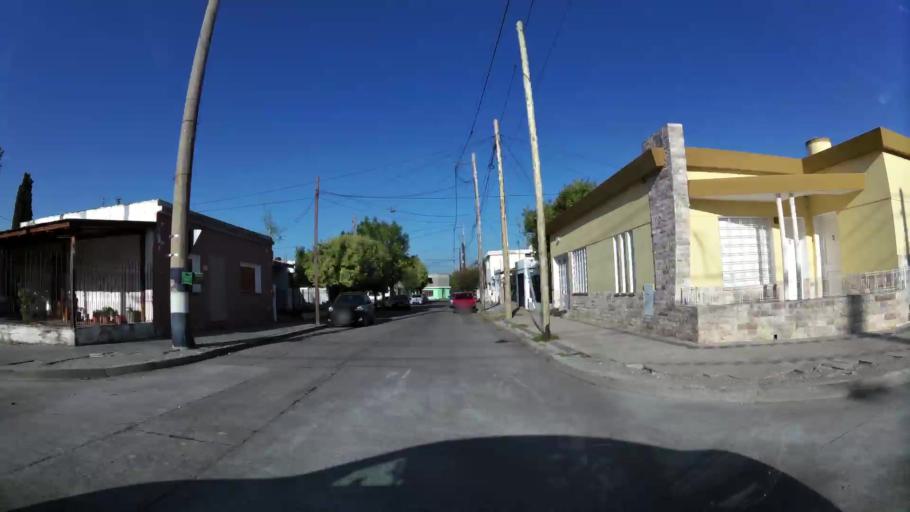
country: AR
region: Cordoba
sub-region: Departamento de Capital
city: Cordoba
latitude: -31.4358
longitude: -64.2480
